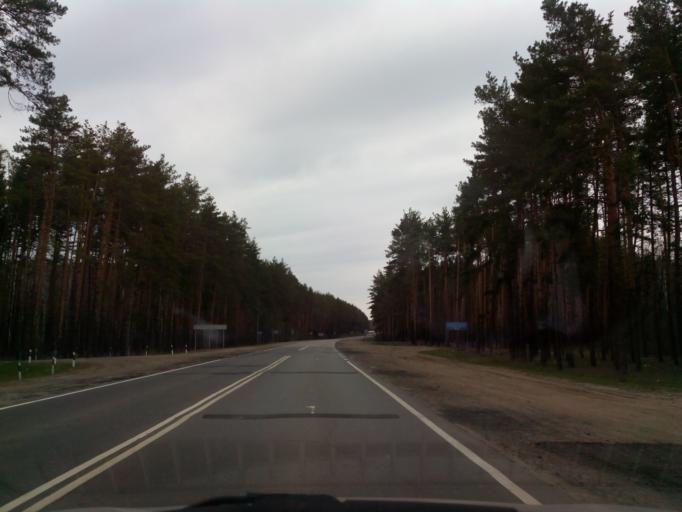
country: RU
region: Tambov
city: Znamenka
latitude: 52.5350
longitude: 41.3557
